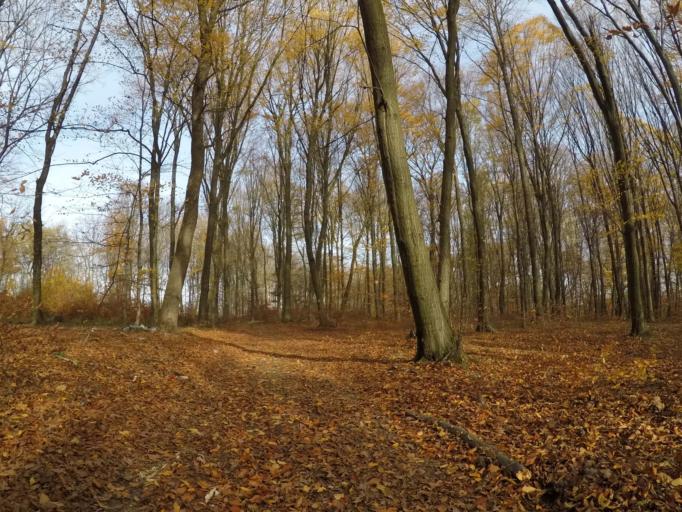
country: SK
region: Presovsky
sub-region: Okres Presov
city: Presov
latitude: 48.9144
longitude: 21.2174
